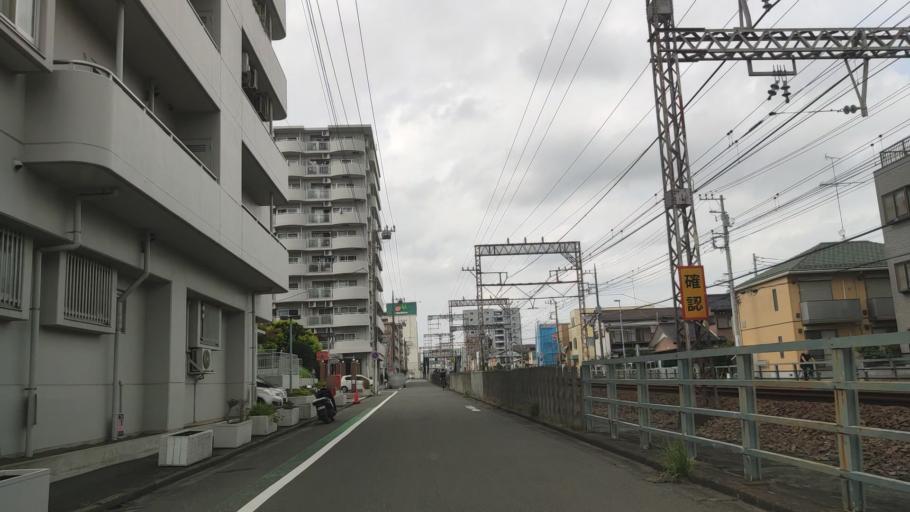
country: JP
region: Kanagawa
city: Minami-rinkan
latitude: 35.4866
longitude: 139.4527
